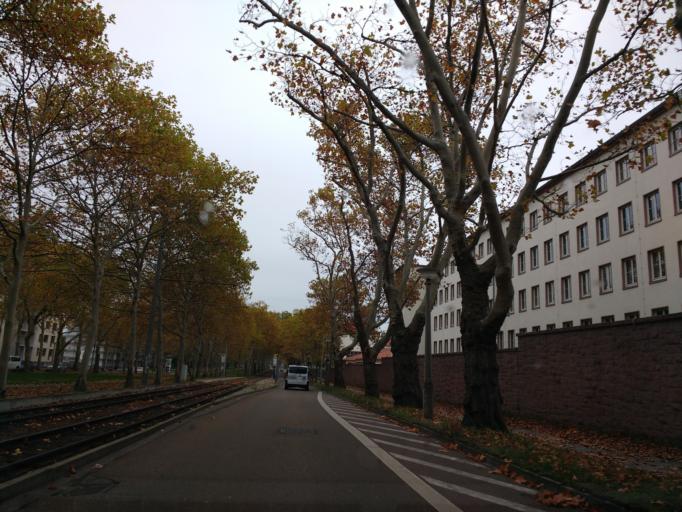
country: DE
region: Saxony-Anhalt
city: Halle Neustadt
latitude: 51.4990
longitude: 11.9345
